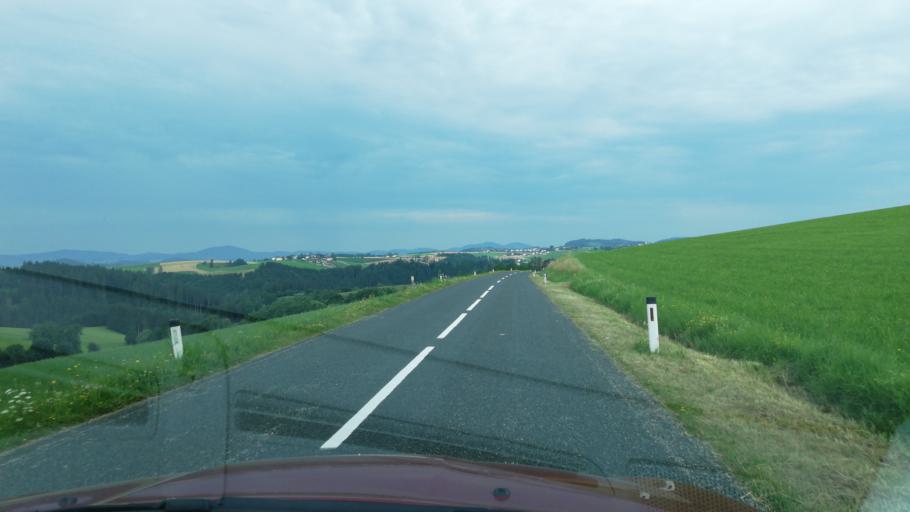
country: AT
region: Upper Austria
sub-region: Politischer Bezirk Rohrbach
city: Kleinzell im Muehlkreis
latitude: 48.4939
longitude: 14.0219
